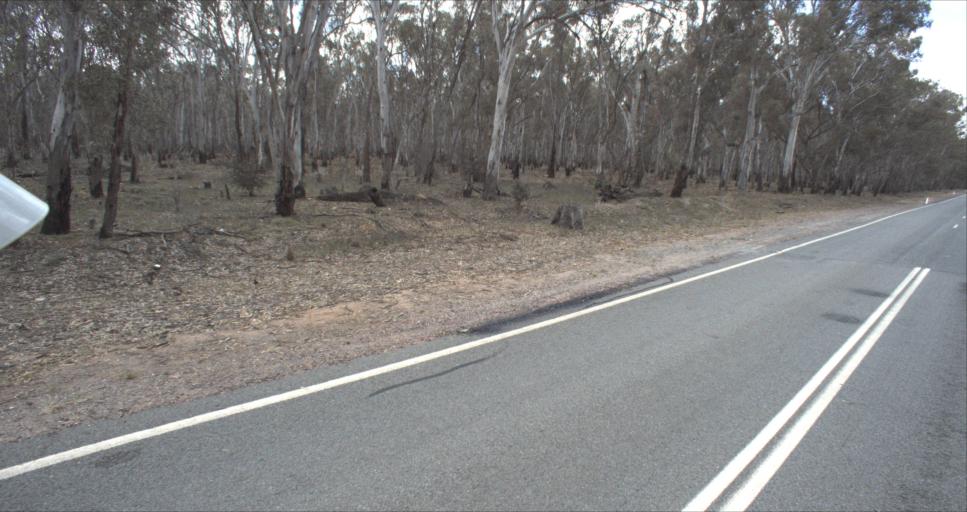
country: AU
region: New South Wales
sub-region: Leeton
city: Leeton
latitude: -34.6293
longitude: 146.3769
